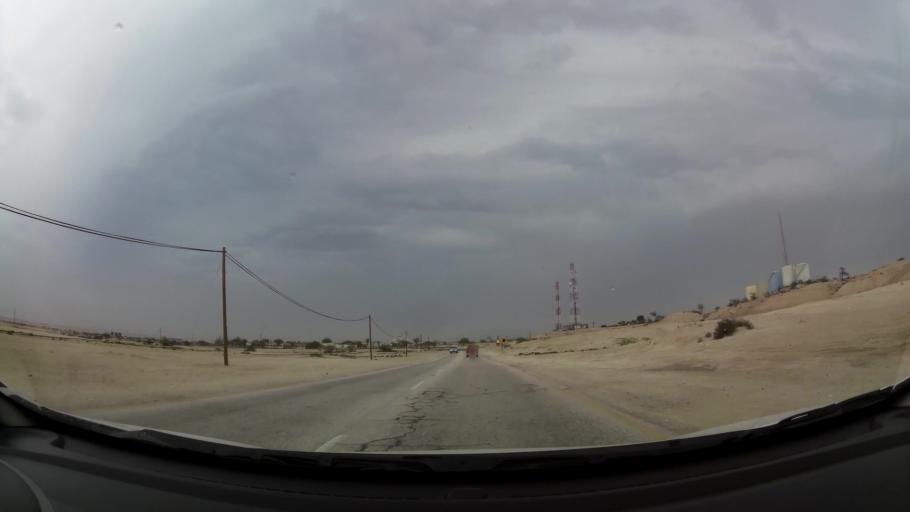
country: BH
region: Central Governorate
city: Dar Kulayb
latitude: 26.0776
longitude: 50.5499
